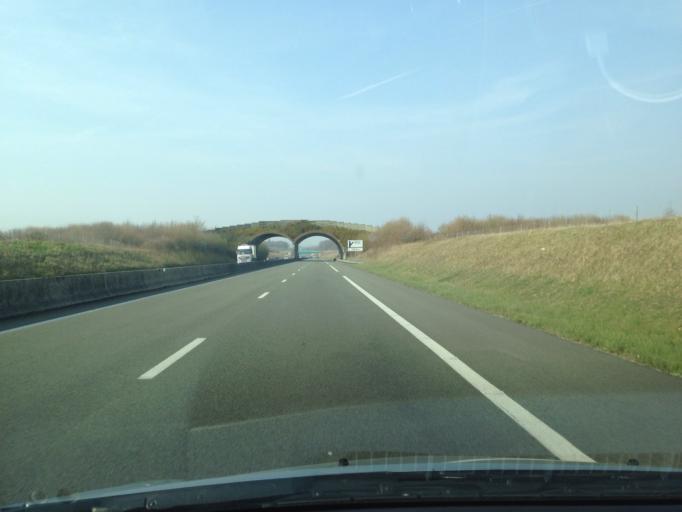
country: FR
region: Picardie
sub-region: Departement de la Somme
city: Nouvion
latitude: 50.2297
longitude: 1.7521
